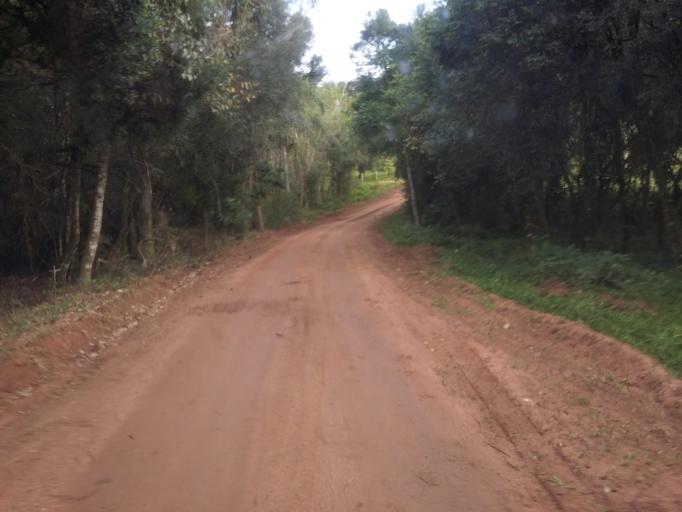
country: BR
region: Rio Grande do Sul
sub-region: Camaqua
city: Camaqua
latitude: -30.7109
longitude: -51.7759
